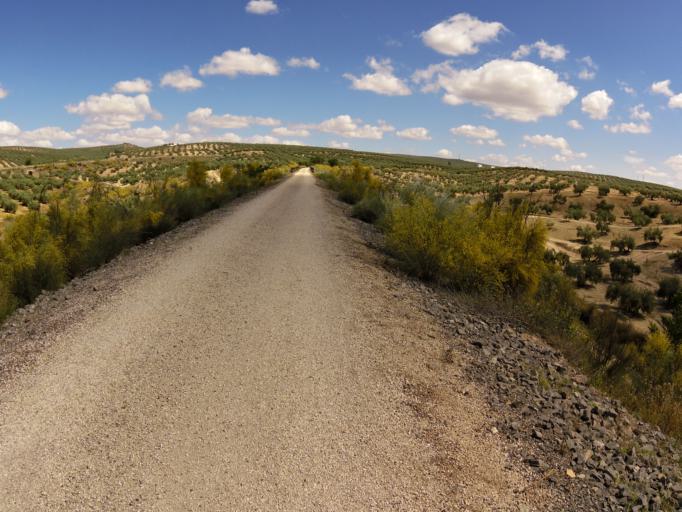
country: ES
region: Andalusia
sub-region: Provincia de Jaen
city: Alcaudete
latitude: 37.6407
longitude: -4.0824
